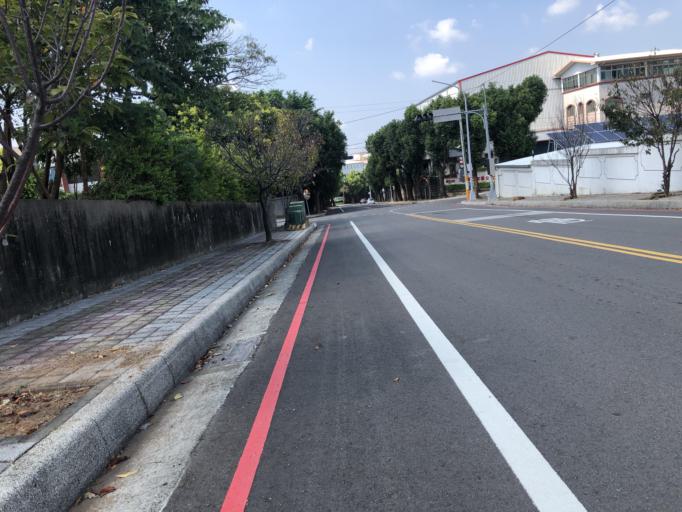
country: TW
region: Taiwan
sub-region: Miaoli
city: Miaoli
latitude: 24.4777
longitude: 120.7935
